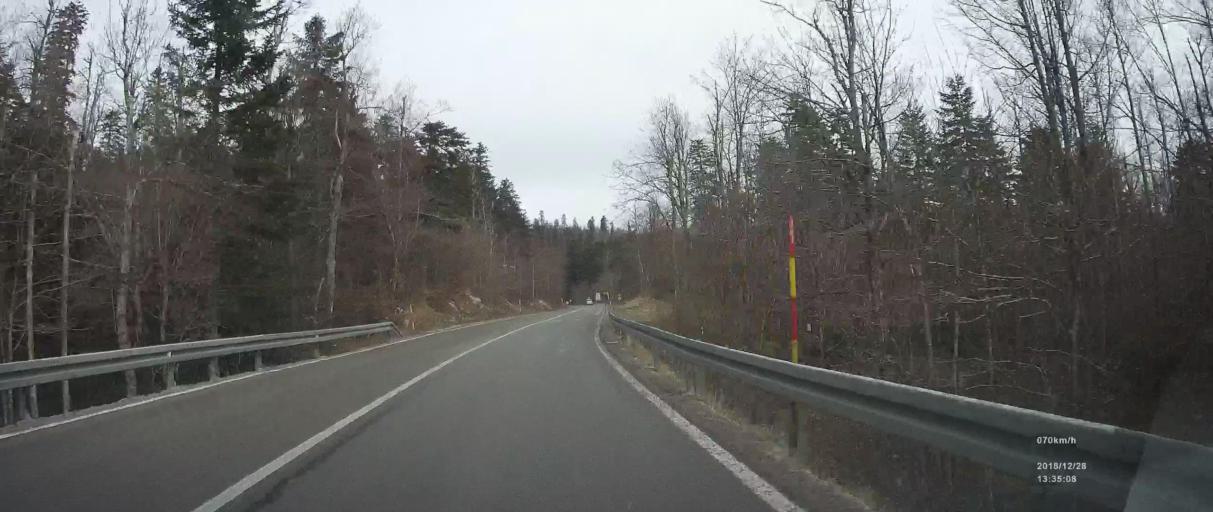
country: HR
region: Primorsko-Goranska
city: Hreljin
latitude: 45.3469
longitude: 14.6898
